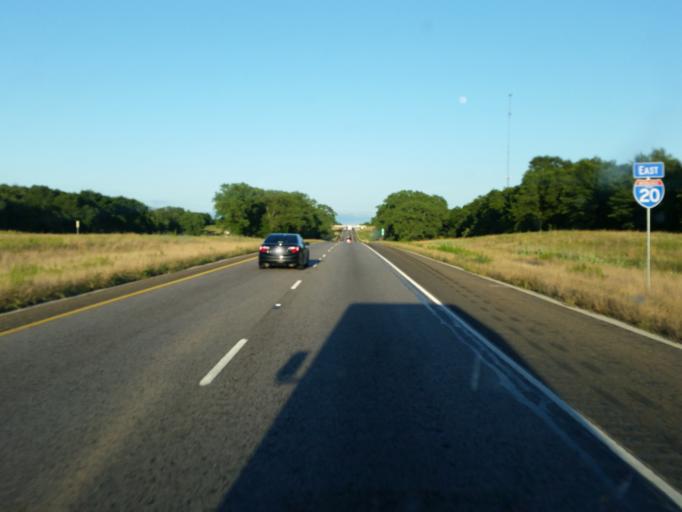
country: US
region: Texas
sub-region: Van Zandt County
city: Wills Point
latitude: 32.6665
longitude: -96.1384
